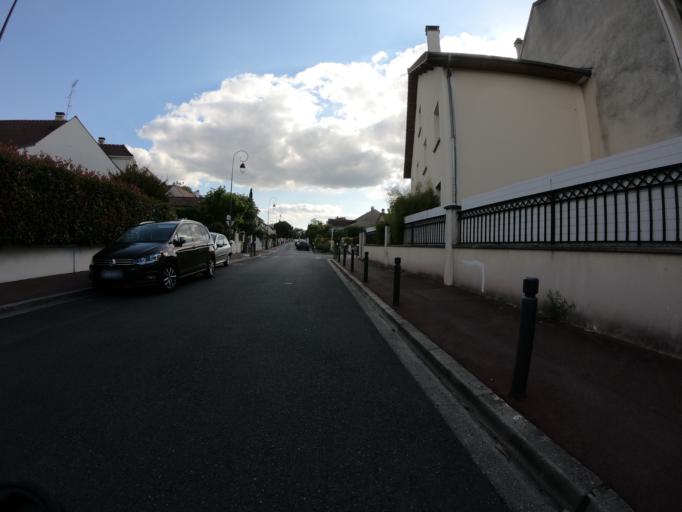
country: FR
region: Ile-de-France
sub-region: Departement des Hauts-de-Seine
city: Antony
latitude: 48.7451
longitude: 2.3093
